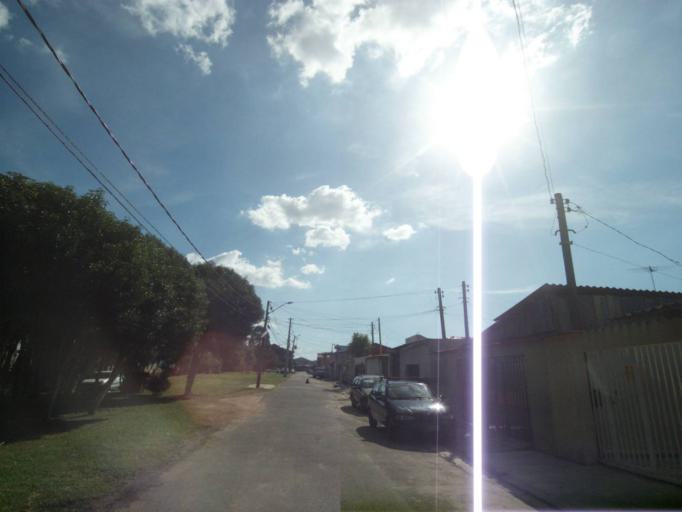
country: BR
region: Parana
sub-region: Pinhais
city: Pinhais
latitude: -25.4534
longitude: -49.2010
